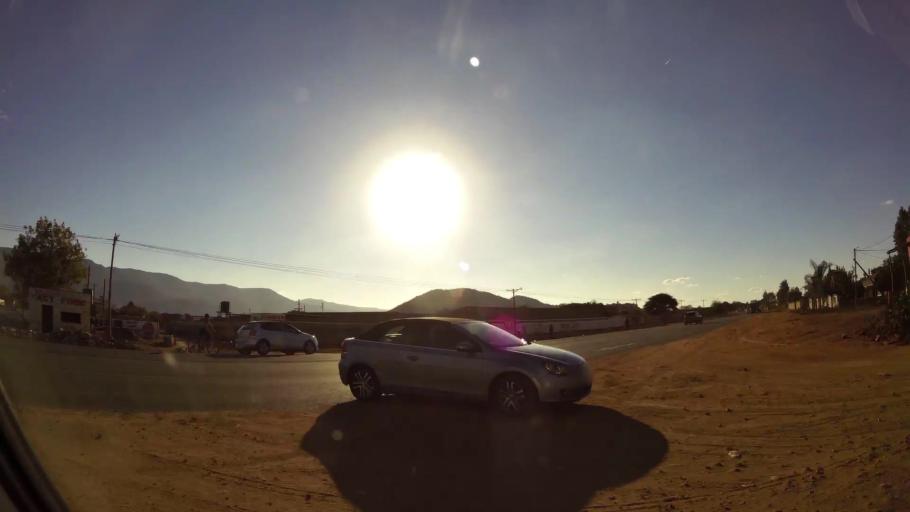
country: ZA
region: Limpopo
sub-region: Waterberg District Municipality
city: Mokopane
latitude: -24.1679
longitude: 28.9847
